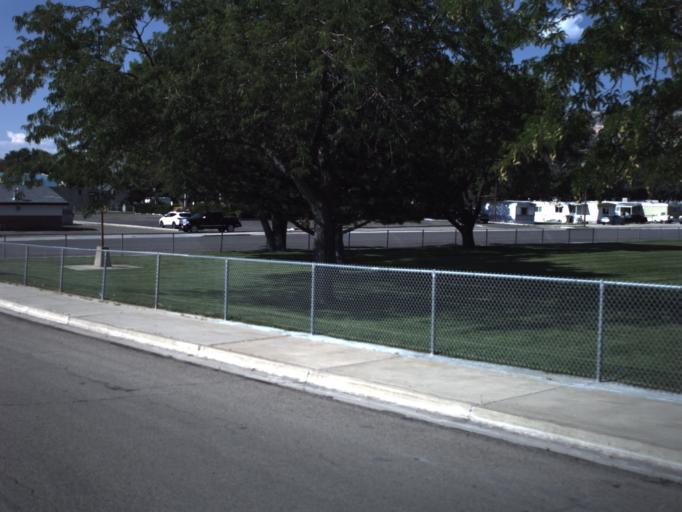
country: US
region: Utah
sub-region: Emery County
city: Ferron
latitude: 39.0922
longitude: -111.1322
